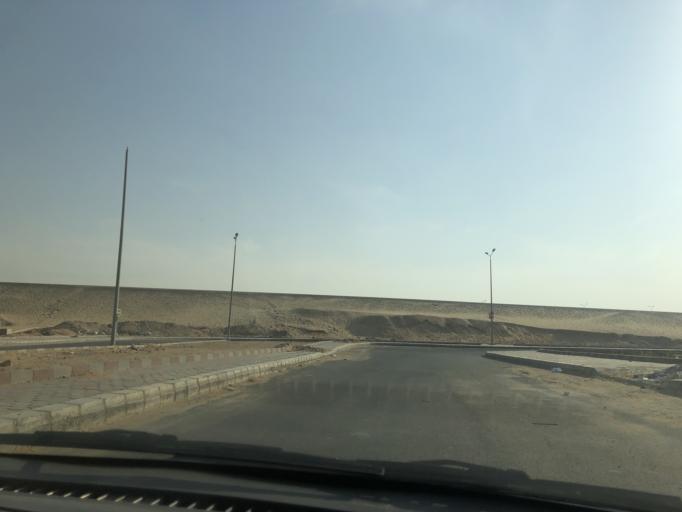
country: EG
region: Al Jizah
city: Madinat Sittah Uktubar
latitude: 29.9038
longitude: 30.9330
